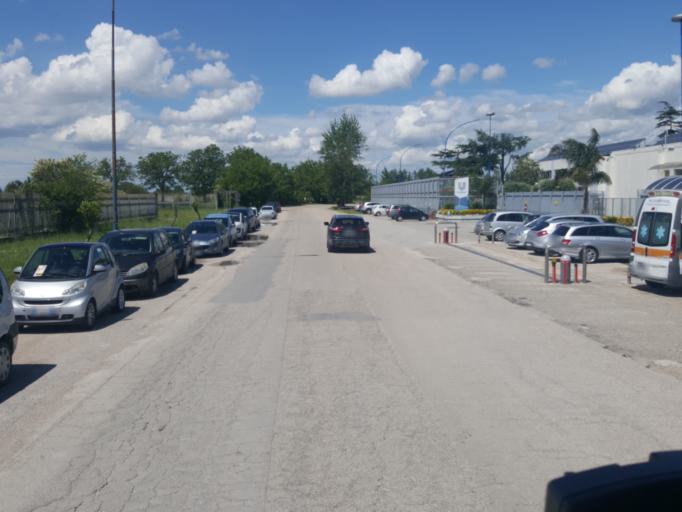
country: IT
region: Campania
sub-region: Provincia di Napoli
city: Pascarola
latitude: 40.9820
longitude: 14.2971
